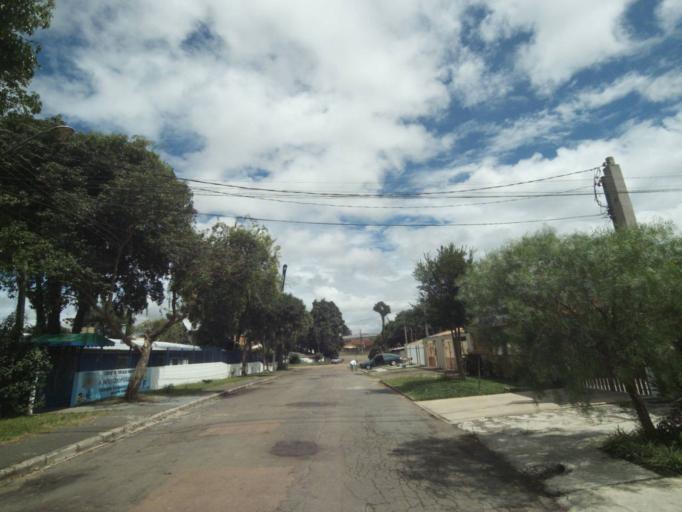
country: BR
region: Parana
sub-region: Curitiba
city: Curitiba
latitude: -25.4810
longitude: -49.2757
